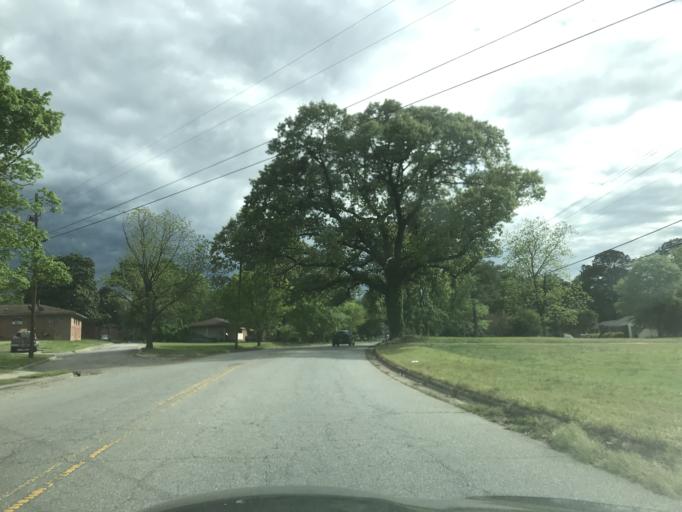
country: US
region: North Carolina
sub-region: Wake County
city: Raleigh
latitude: 35.7744
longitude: -78.5918
